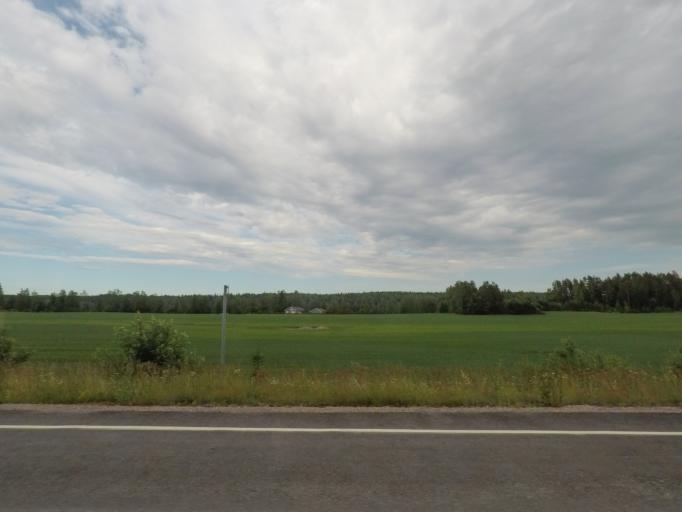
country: FI
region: Uusimaa
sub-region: Helsinki
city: Maentsaelae
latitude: 60.7535
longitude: 25.4331
